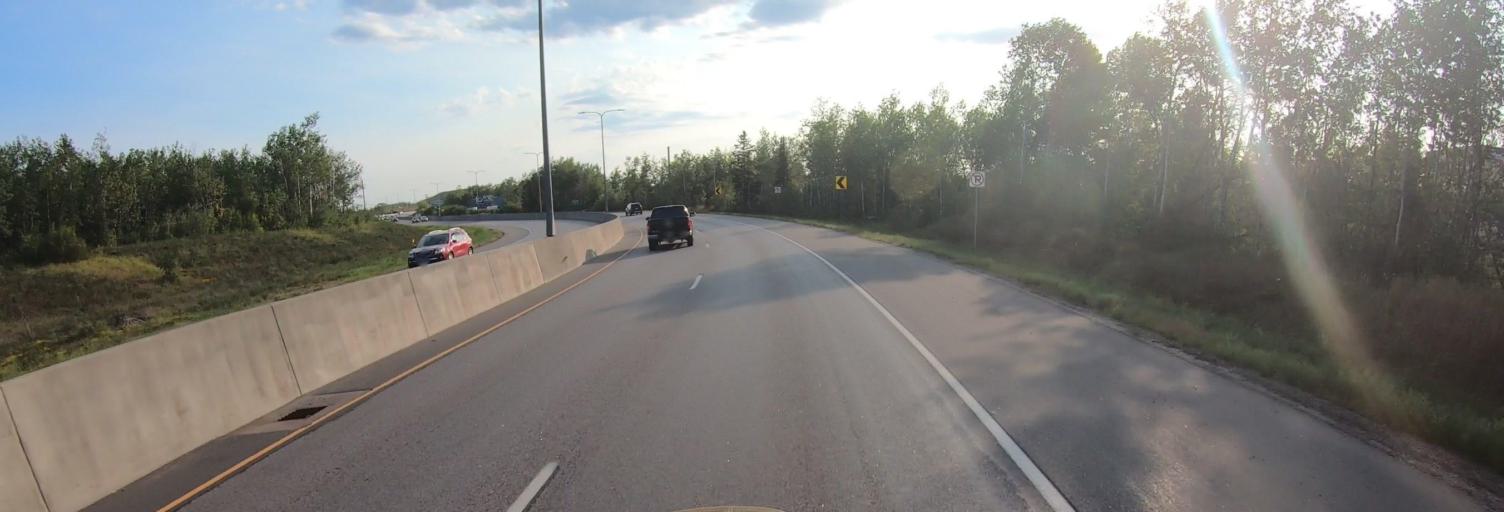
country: US
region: Minnesota
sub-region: Saint Louis County
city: Virginia
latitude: 47.5155
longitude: -92.5270
